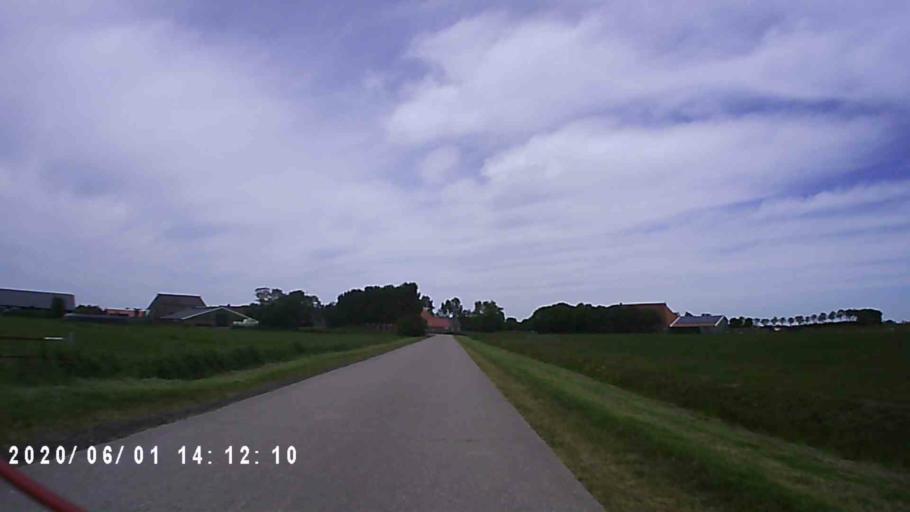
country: NL
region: Friesland
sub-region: Gemeente Littenseradiel
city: Winsum
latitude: 53.1292
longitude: 5.6502
